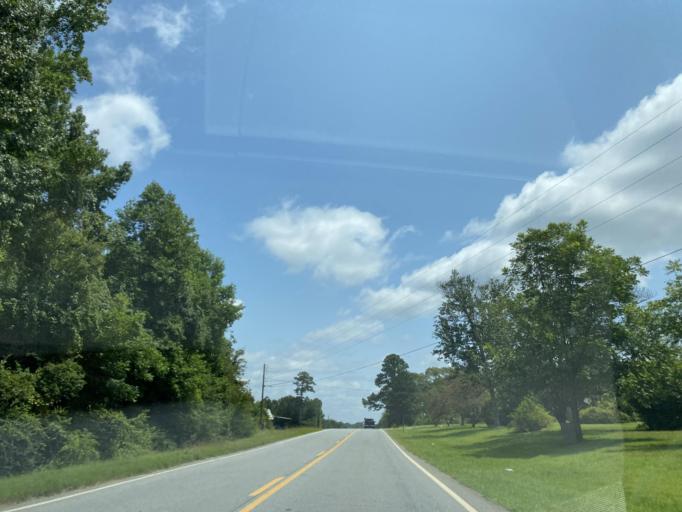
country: US
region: Georgia
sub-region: Telfair County
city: Helena
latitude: 32.0203
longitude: -83.0488
